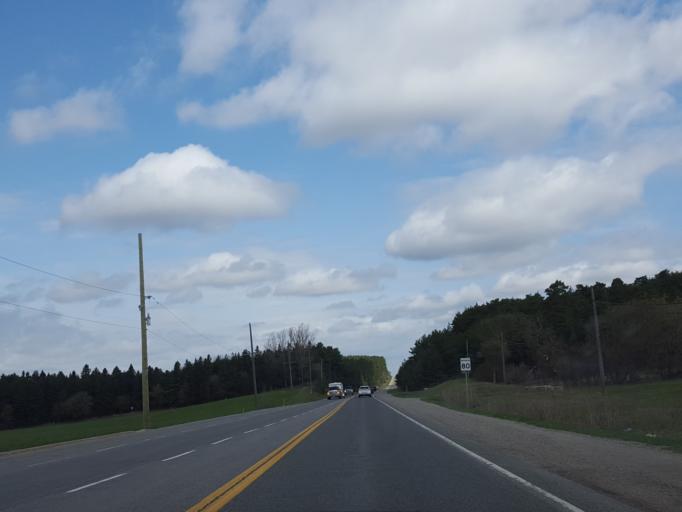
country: CA
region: Ontario
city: Newmarket
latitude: 44.0755
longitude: -79.3061
